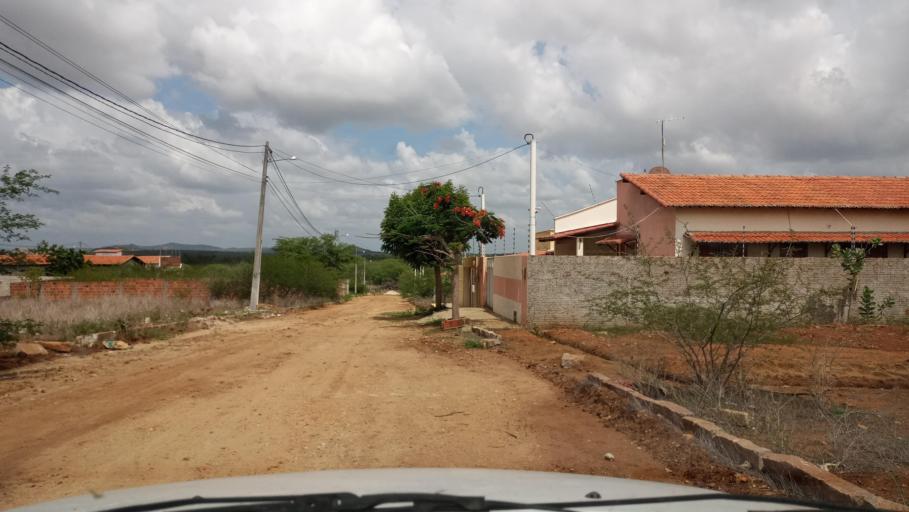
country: BR
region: Rio Grande do Norte
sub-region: Tangara
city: Tangara
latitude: -6.1128
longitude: -35.7164
